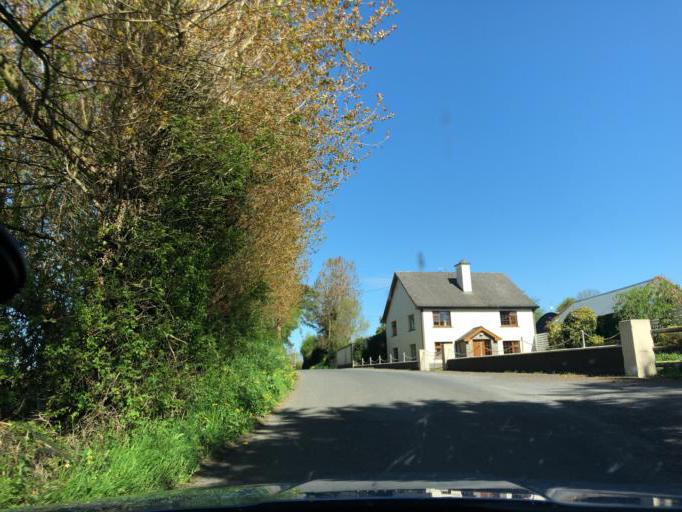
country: IE
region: Connaught
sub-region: County Galway
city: Portumna
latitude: 53.1512
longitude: -8.2932
